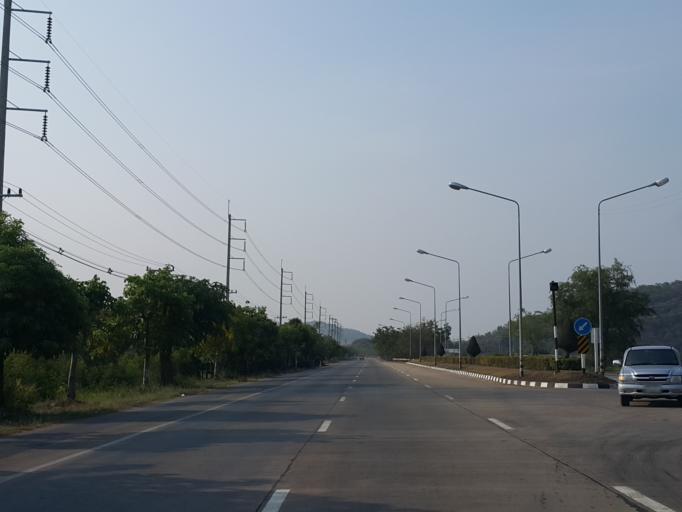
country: TH
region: Suphan Buri
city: Doembang Nangbuat
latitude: 14.8245
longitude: 100.1148
